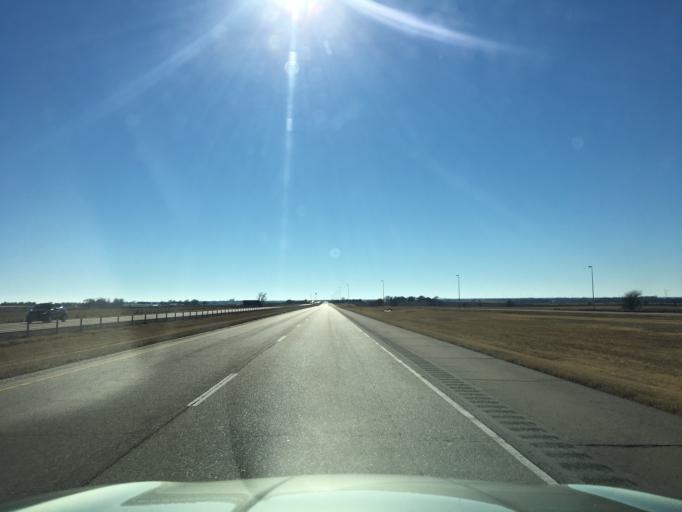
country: US
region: Oklahoma
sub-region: Kay County
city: Blackwell
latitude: 36.9824
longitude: -97.3458
